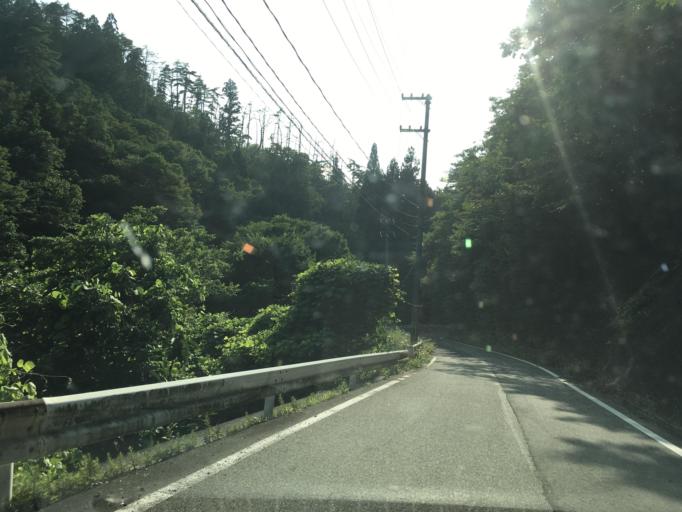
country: JP
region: Iwate
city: Ofunato
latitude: 38.9158
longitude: 141.5993
